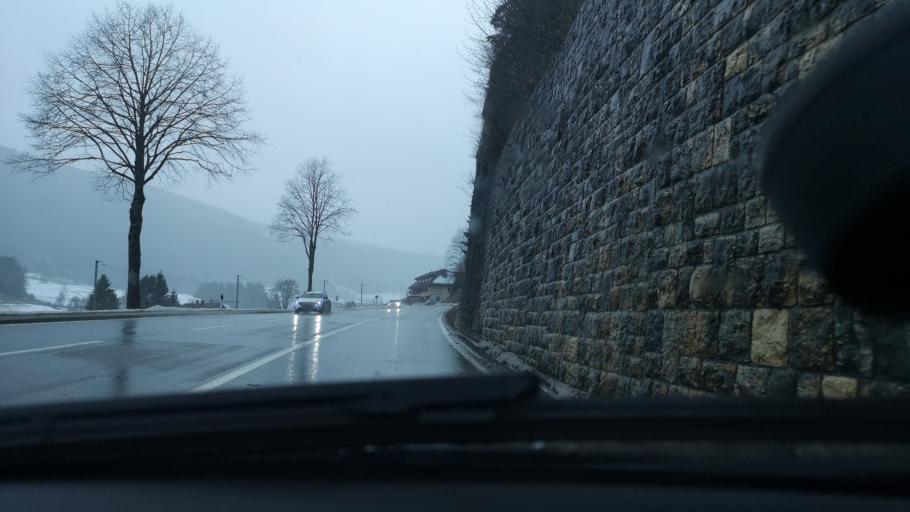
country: CH
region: Neuchatel
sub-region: Val-de-Travers District
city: Travers
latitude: 46.9479
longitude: 6.6928
